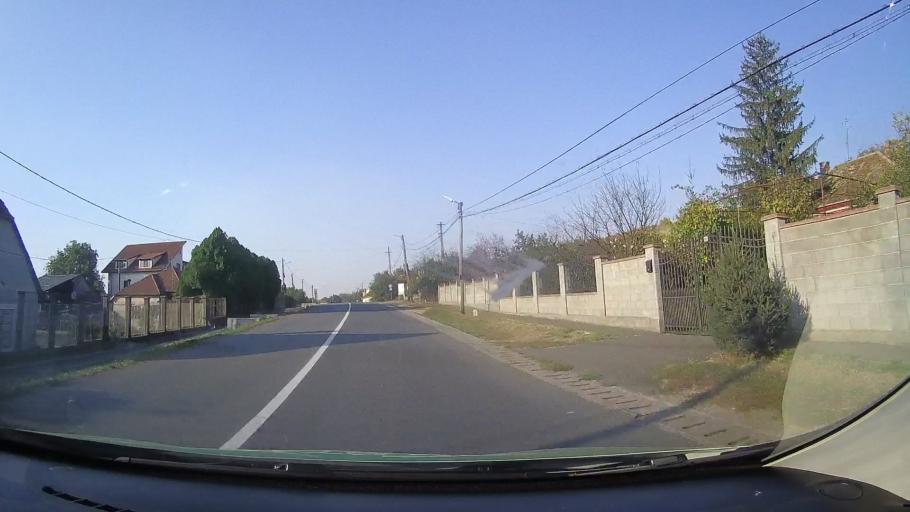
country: RO
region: Arad
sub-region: Comuna Ghioroc
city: Cuvin
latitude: 46.1590
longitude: 21.5930
